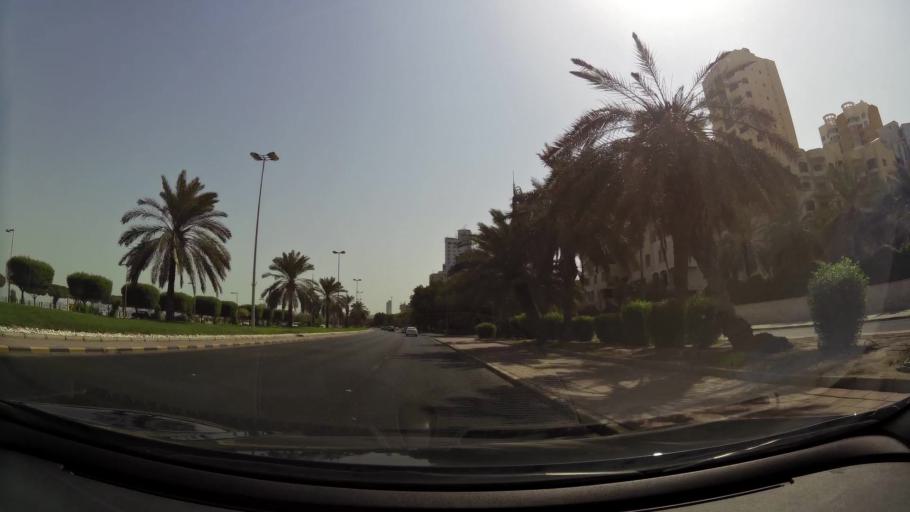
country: KW
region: Muhafazat Hawalli
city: Hawalli
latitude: 29.3532
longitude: 48.0293
